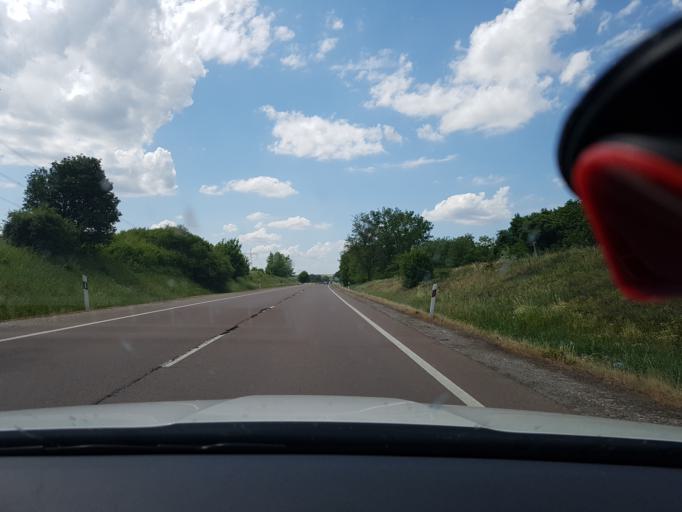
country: HU
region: Heves
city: Karacsond
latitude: 47.7401
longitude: 20.1165
